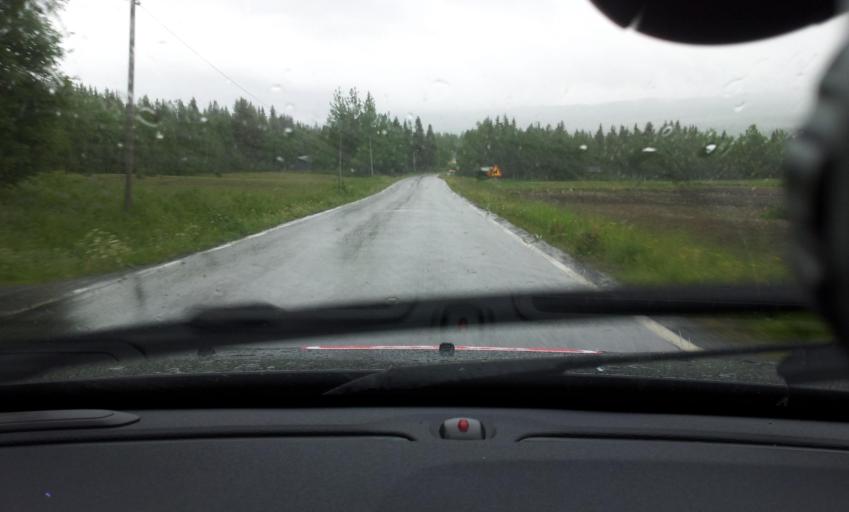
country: SE
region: Jaemtland
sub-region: Are Kommun
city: Are
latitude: 63.3129
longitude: 13.2024
